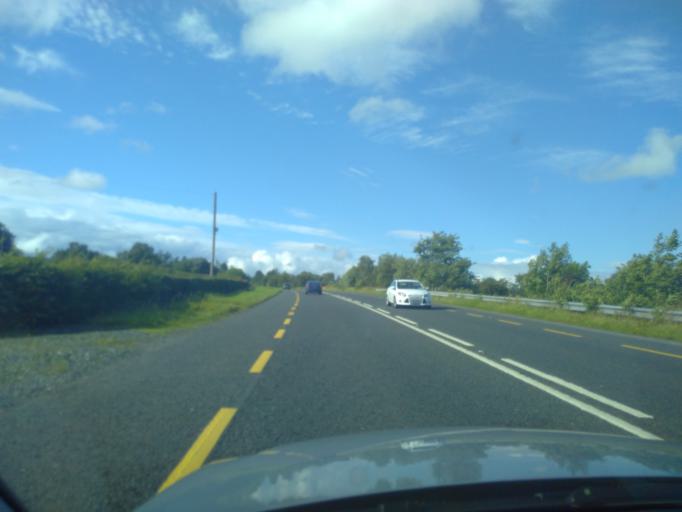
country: IE
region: Ulster
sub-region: County Donegal
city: Ballybofey
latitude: 54.8519
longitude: -7.7501
